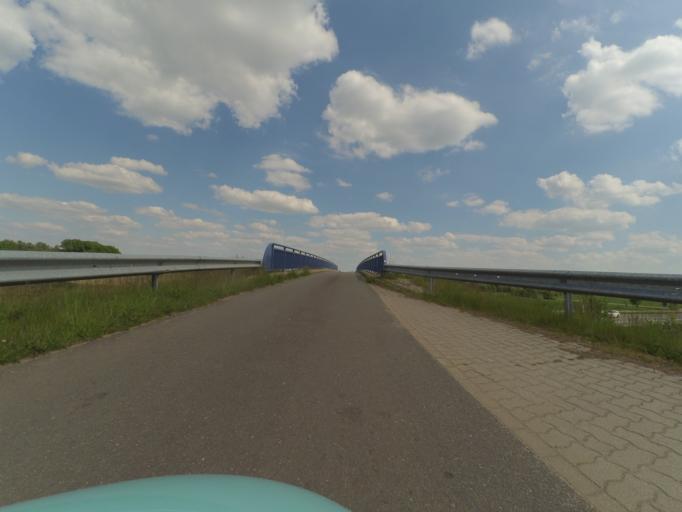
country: DE
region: Lower Saxony
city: Adelheidsdorf
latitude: 52.5436
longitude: 10.0711
